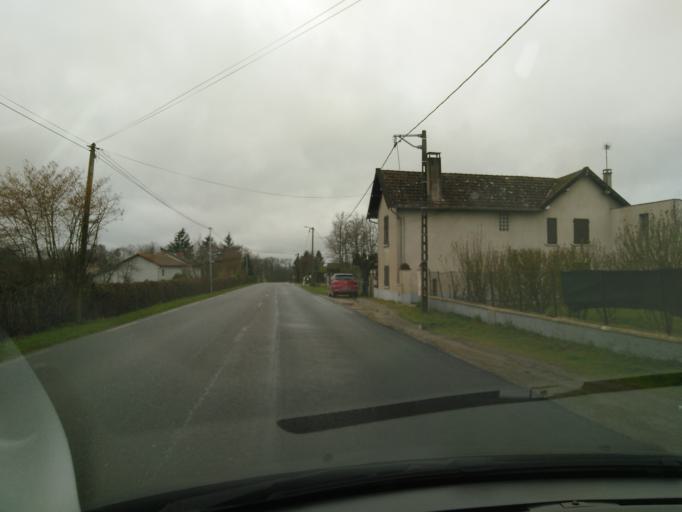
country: FR
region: Limousin
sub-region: Departement de la Haute-Vienne
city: Solignac
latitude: 45.7204
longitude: 1.2521
